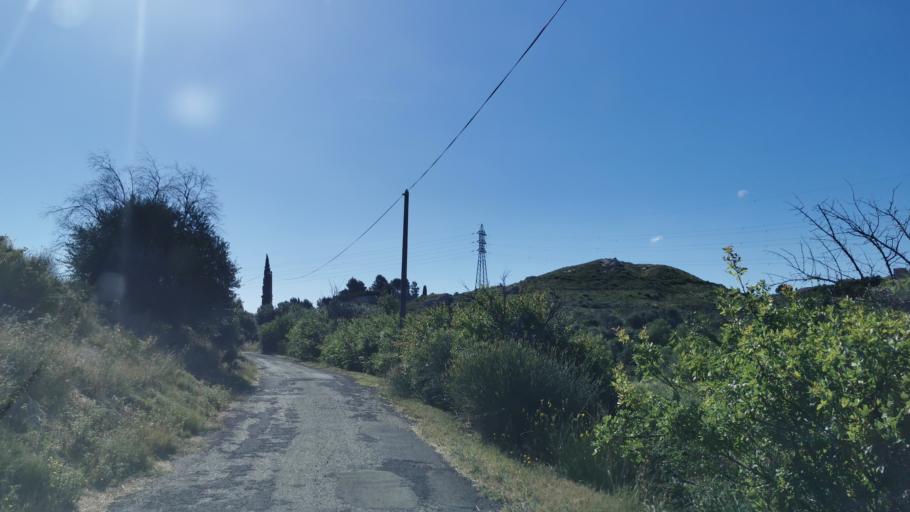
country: FR
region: Languedoc-Roussillon
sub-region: Departement de l'Aude
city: Narbonne
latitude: 43.1699
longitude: 2.9726
